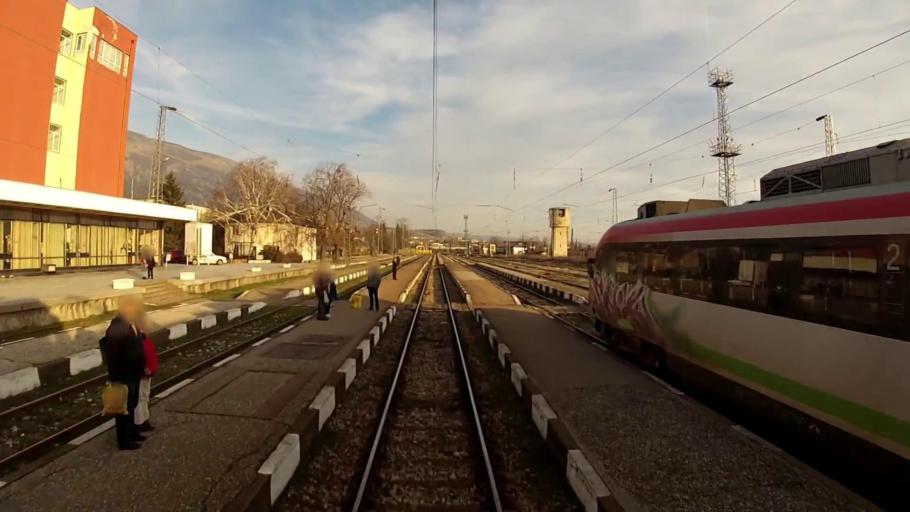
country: BG
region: Plovdiv
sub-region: Obshtina Karlovo
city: Karlovo
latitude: 42.6316
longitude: 24.7988
